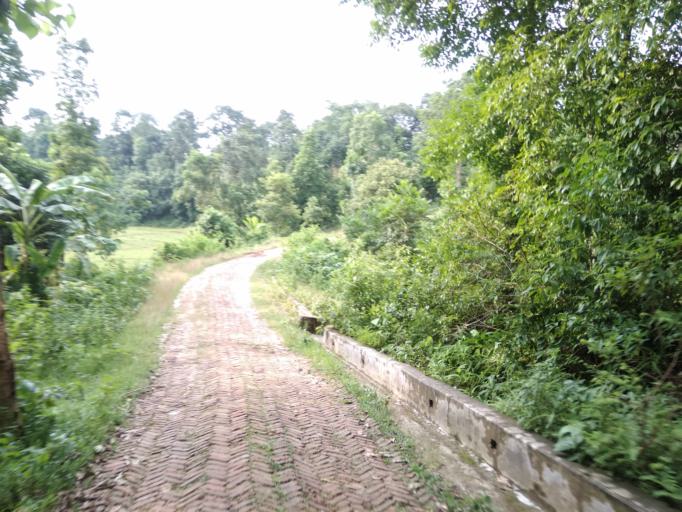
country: BD
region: Chittagong
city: Manikchari
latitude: 22.9260
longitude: 91.9120
